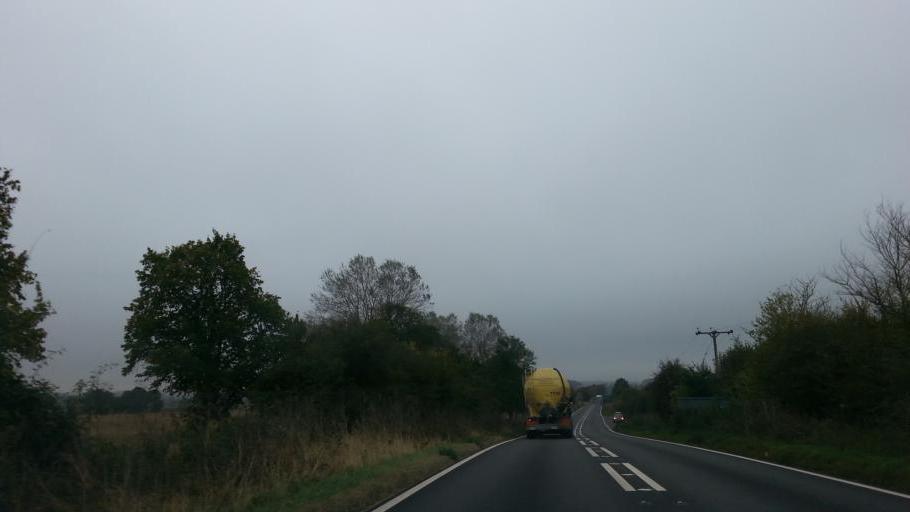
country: GB
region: England
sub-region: Northamptonshire
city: Oundle
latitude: 52.4367
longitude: -0.4766
